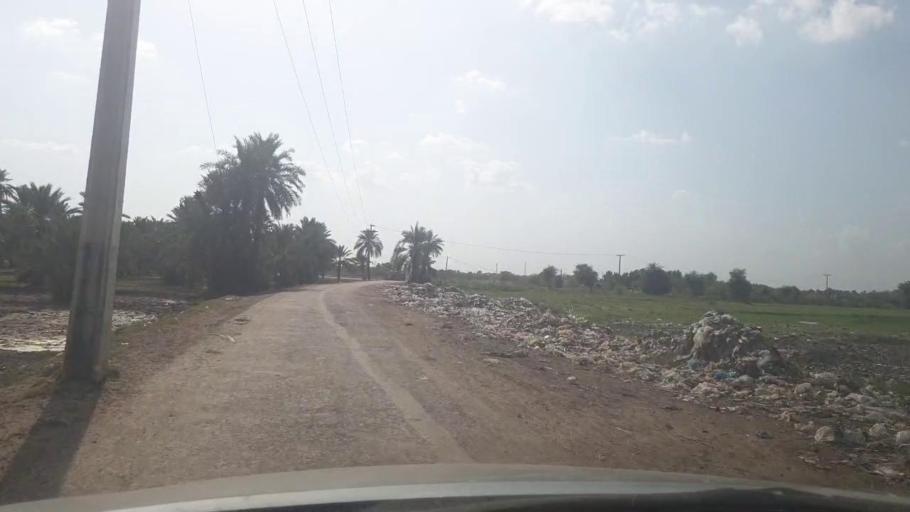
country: PK
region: Sindh
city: Khairpur
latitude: 27.5292
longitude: 68.7749
